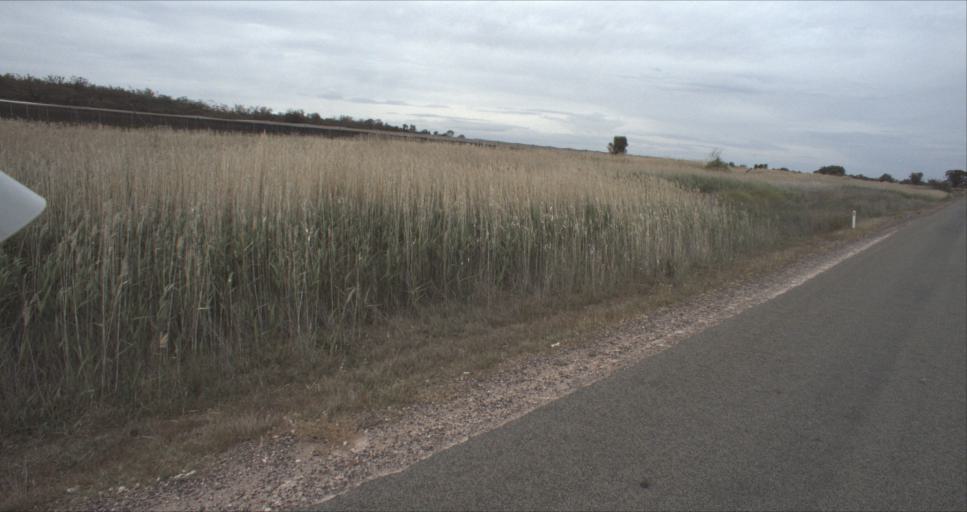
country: AU
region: New South Wales
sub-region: Leeton
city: Leeton
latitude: -34.4306
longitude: 146.3775
